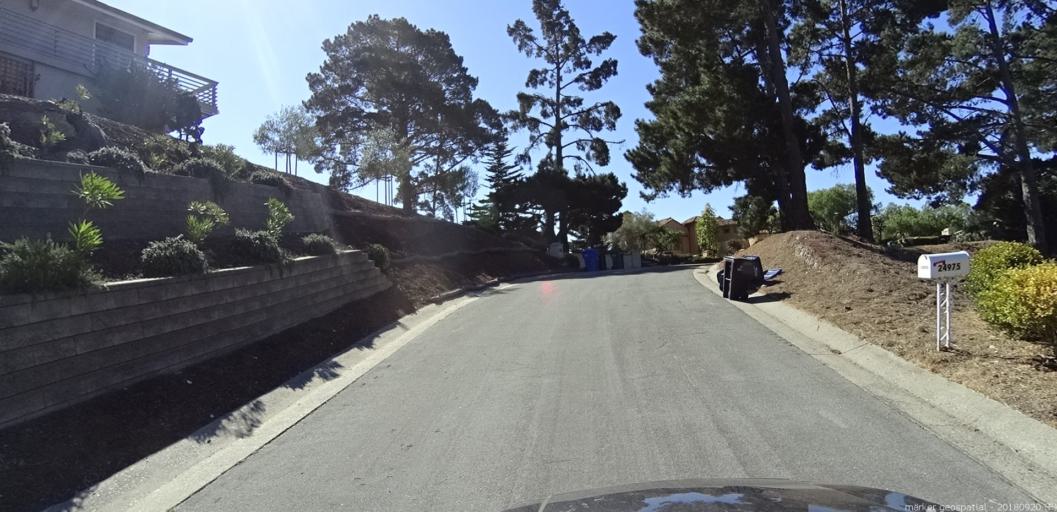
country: US
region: California
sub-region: Monterey County
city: Carmel-by-the-Sea
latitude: 36.5607
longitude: -121.8996
